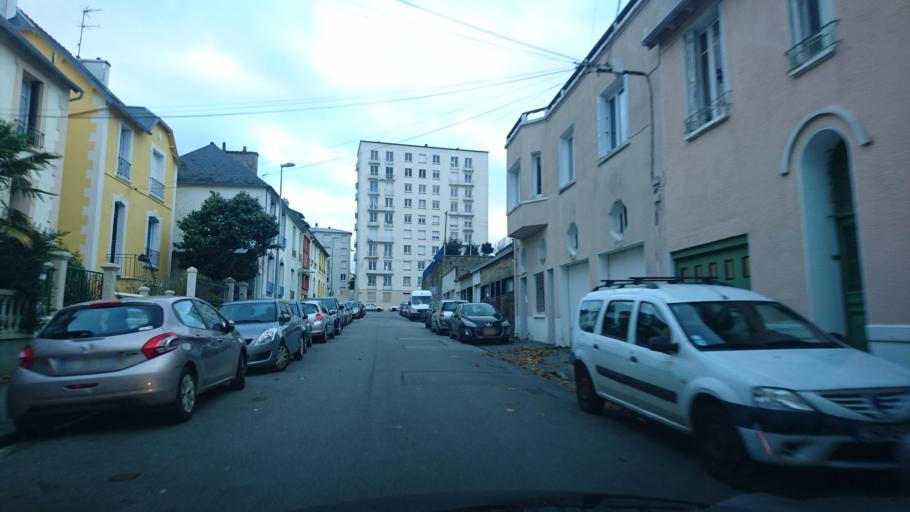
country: FR
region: Brittany
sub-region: Departement du Finistere
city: Brest
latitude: 48.3894
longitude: -4.4790
